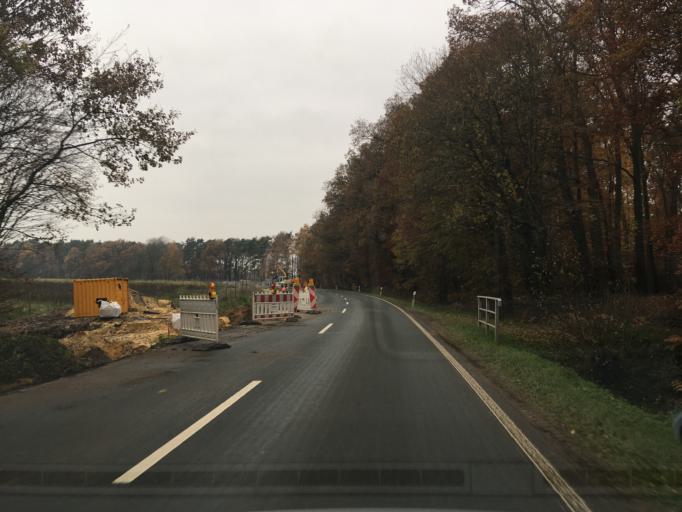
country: DE
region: North Rhine-Westphalia
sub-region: Regierungsbezirk Munster
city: Legden
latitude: 52.0290
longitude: 7.0728
